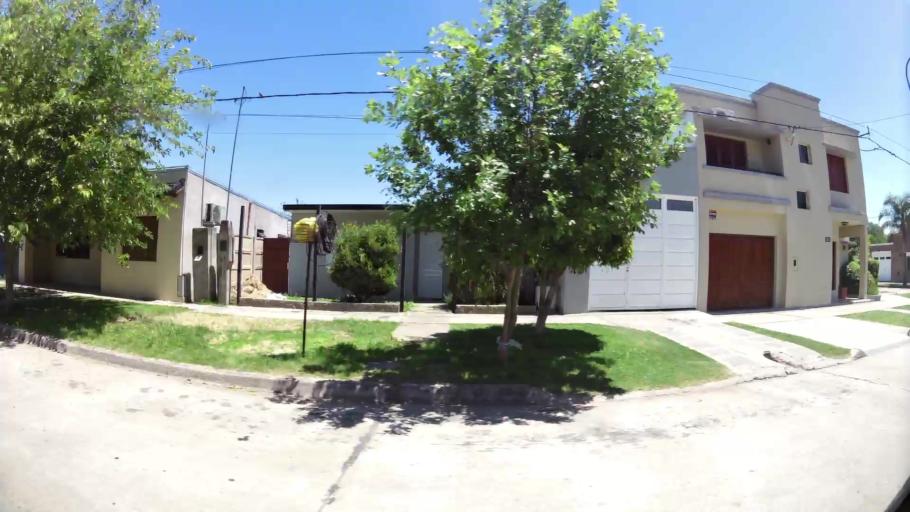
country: AR
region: Santa Fe
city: Rafaela
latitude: -31.2548
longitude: -61.4570
